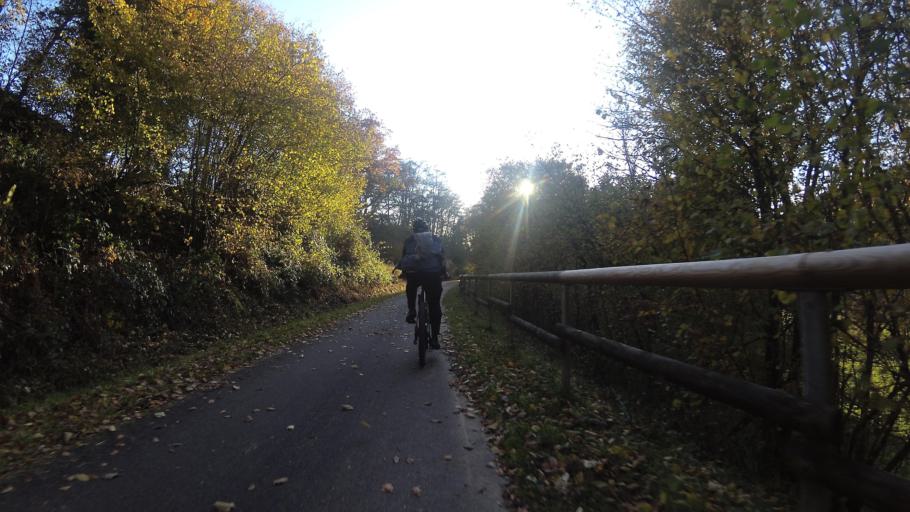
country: DE
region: Rheinland-Pfalz
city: Heddert
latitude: 49.6434
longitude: 6.7277
